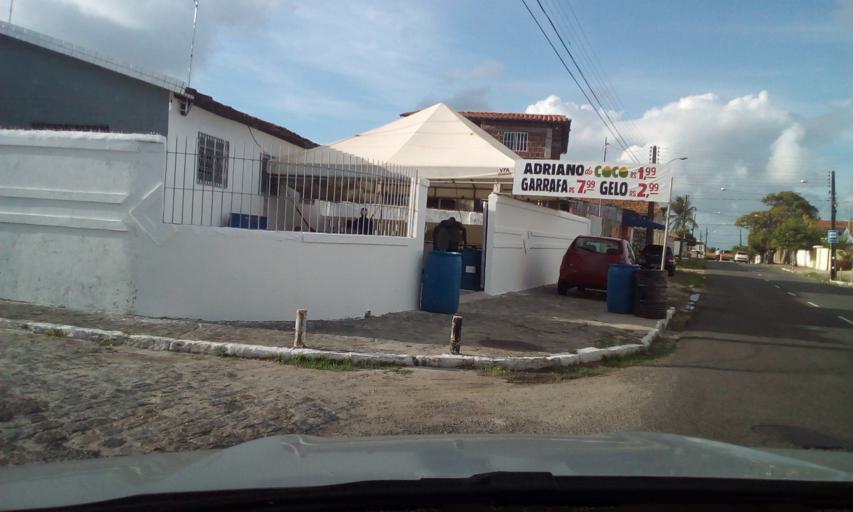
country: BR
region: Paraiba
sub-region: Joao Pessoa
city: Joao Pessoa
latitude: -7.1023
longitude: -34.8557
